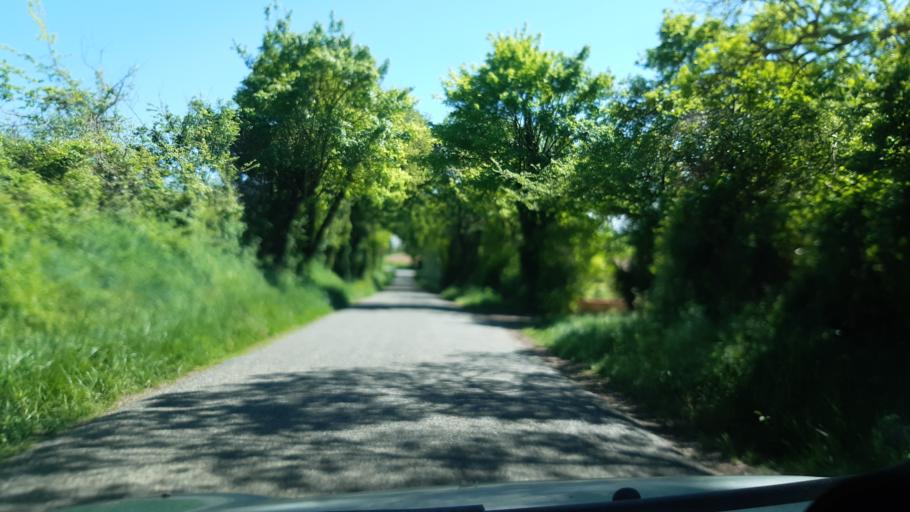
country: FR
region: Midi-Pyrenees
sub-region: Departement du Gers
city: Samatan
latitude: 43.5099
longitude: 1.0131
